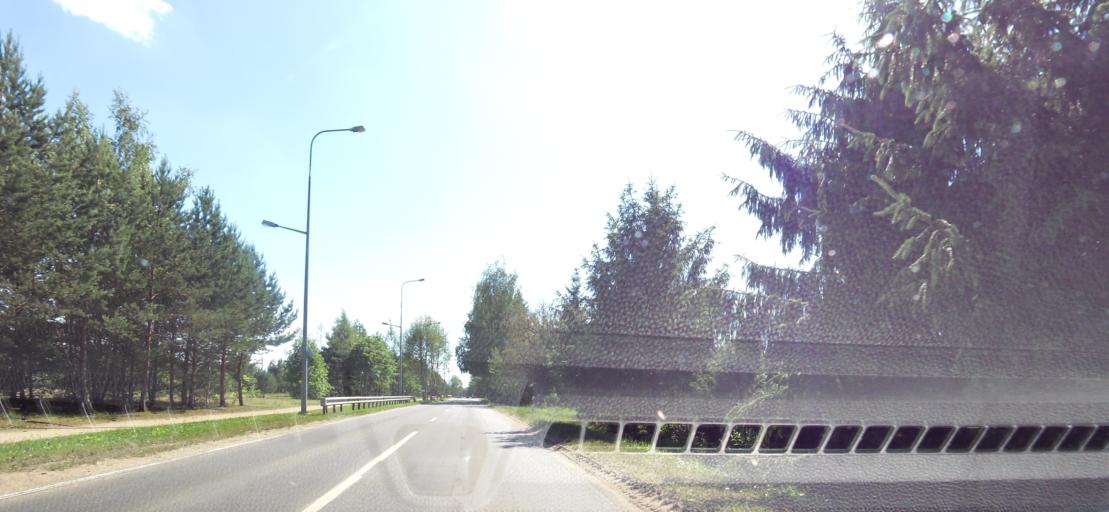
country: LT
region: Vilnius County
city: Rasos
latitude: 54.7846
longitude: 25.3461
